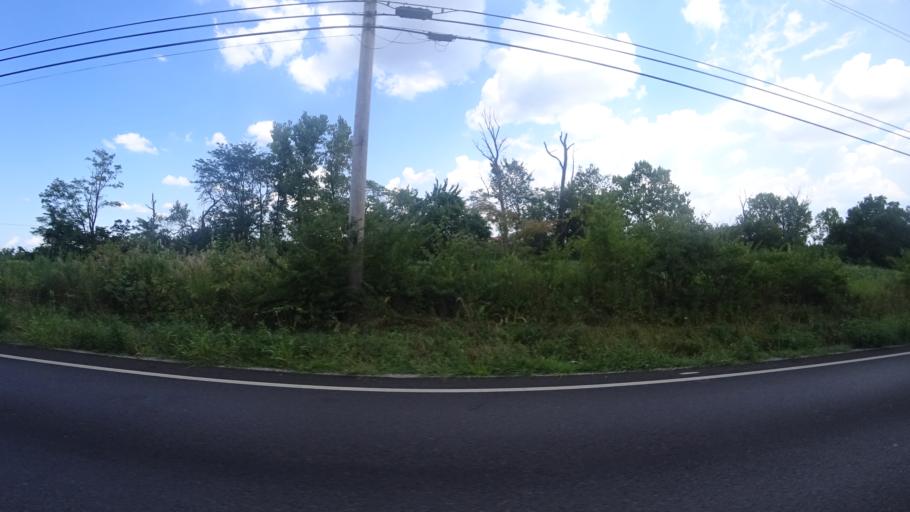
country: US
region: Ohio
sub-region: Butler County
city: Hamilton
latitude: 39.4391
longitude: -84.6088
